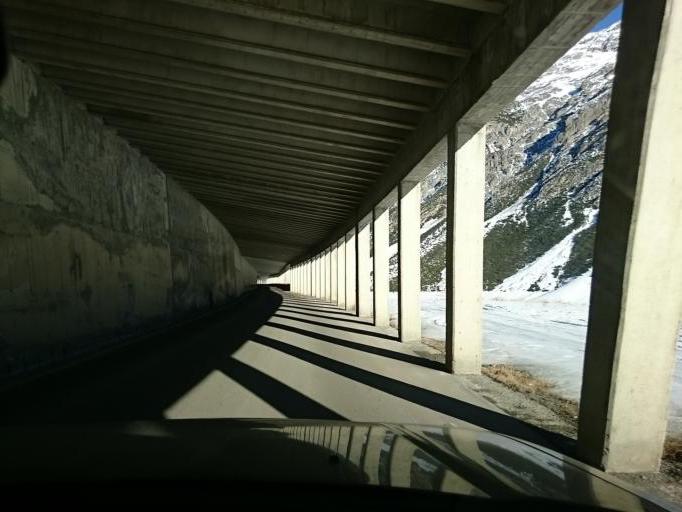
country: IT
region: Lombardy
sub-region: Provincia di Sondrio
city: Livigno
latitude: 46.5686
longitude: 10.1586
